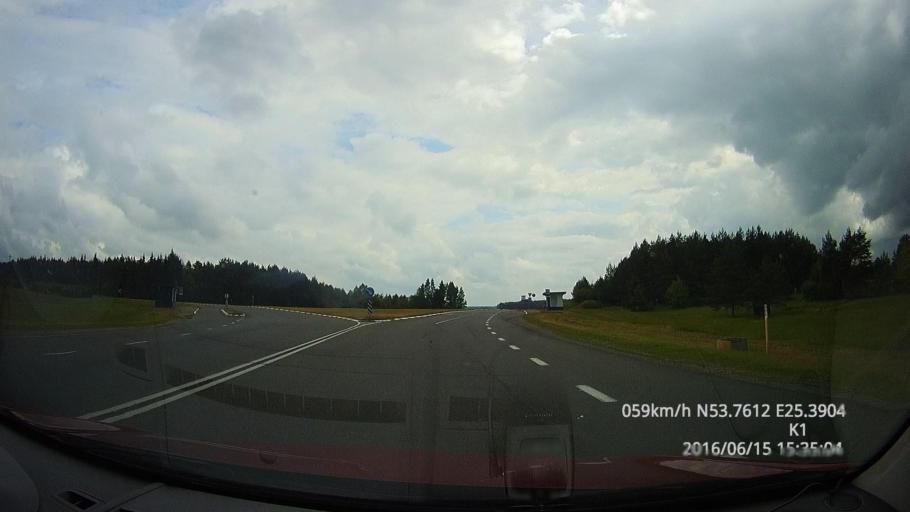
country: BY
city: Berezovka
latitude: 53.7608
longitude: 25.3906
